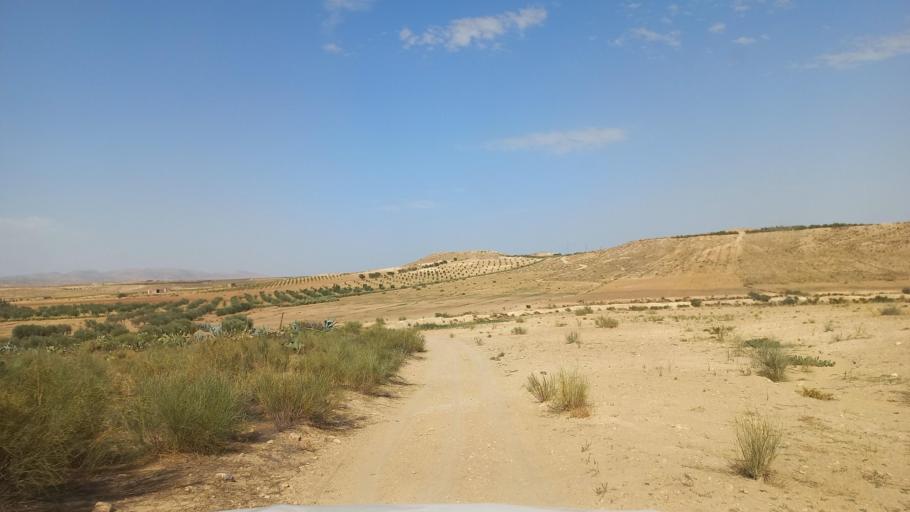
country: TN
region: Al Qasrayn
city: Kasserine
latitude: 35.2790
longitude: 8.9723
